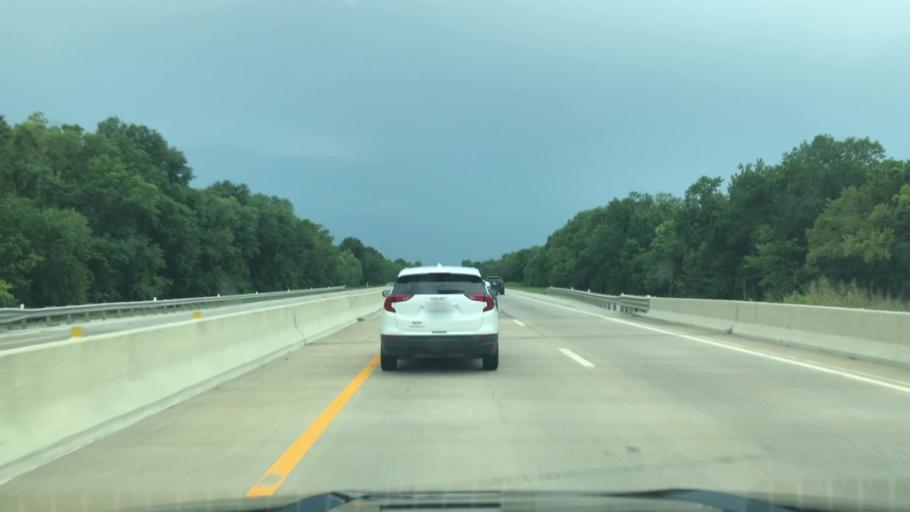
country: US
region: Oklahoma
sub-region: Rogers County
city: Chelsea
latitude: 36.4561
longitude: -95.3571
